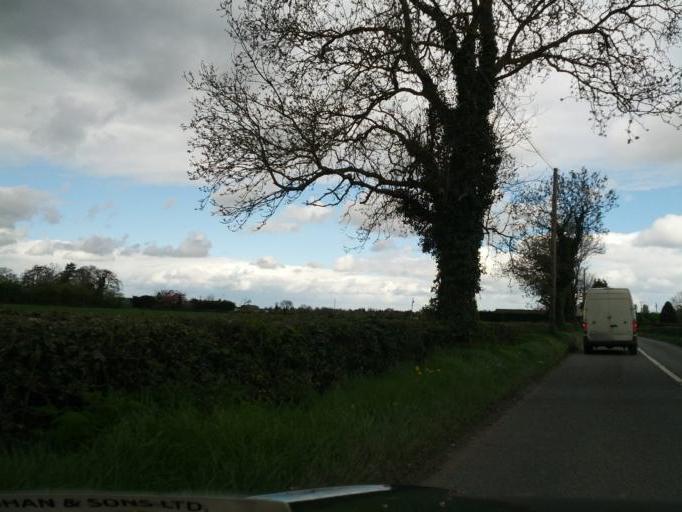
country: IE
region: Leinster
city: Lucan
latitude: 53.3726
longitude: -6.4592
